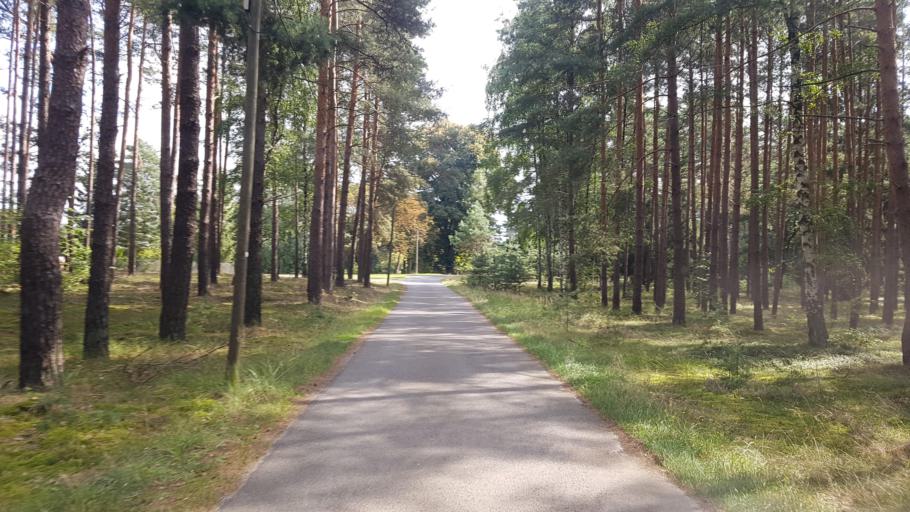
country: DE
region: Brandenburg
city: Hohenbucko
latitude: 51.7522
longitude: 13.5508
